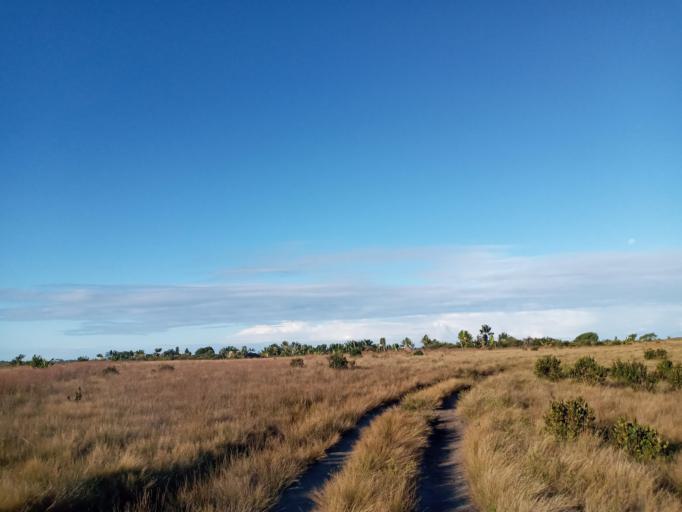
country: MG
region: Anosy
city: Fort Dauphin
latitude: -24.4304
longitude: 47.2951
